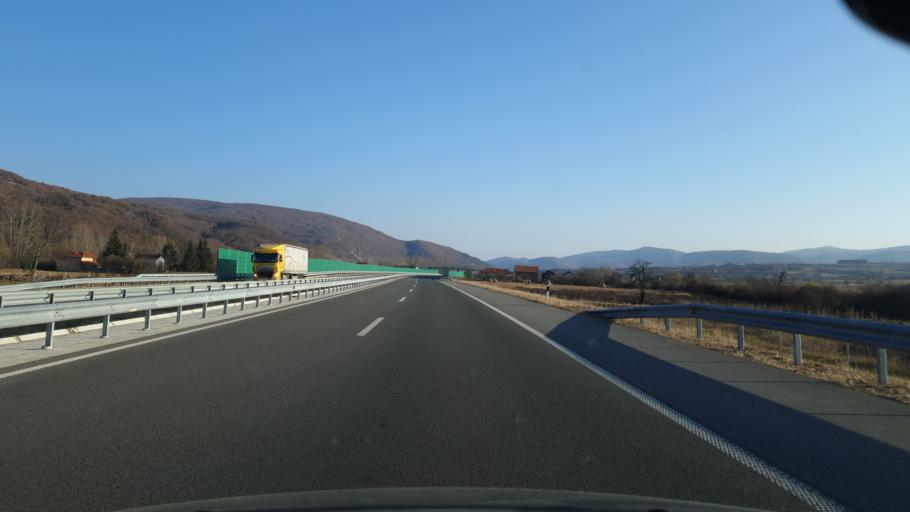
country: RS
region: Central Serbia
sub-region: Pirotski Okrug
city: Dimitrovgrad
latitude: 43.0492
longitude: 22.7019
